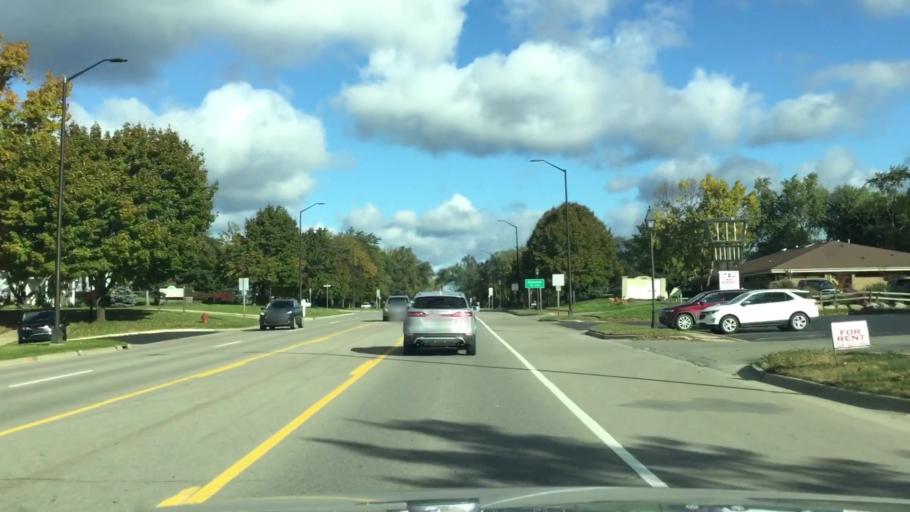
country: US
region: Michigan
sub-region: Oakland County
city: Clarkston
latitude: 42.7249
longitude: -83.4187
